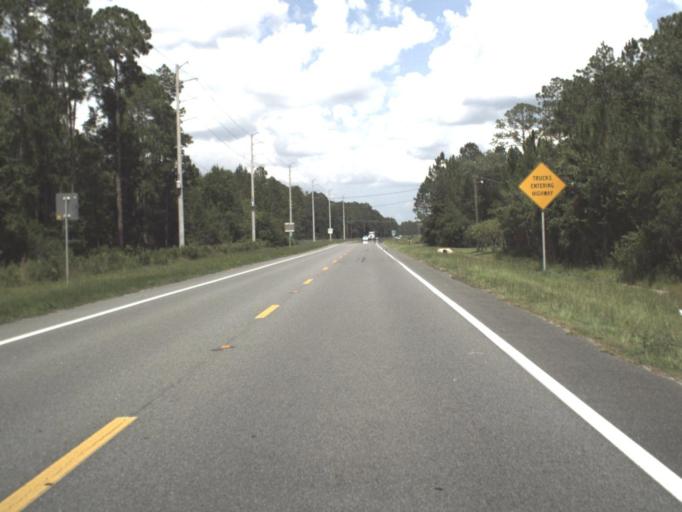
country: US
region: Florida
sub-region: Bradford County
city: Starke
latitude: 29.9563
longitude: -82.0511
